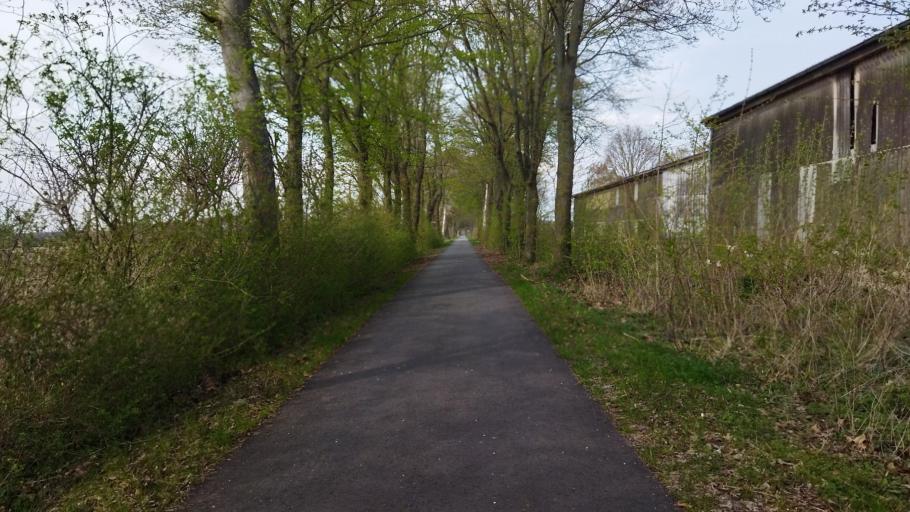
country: DE
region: Lower Saxony
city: Raddestorf
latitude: 52.4211
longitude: 8.9675
